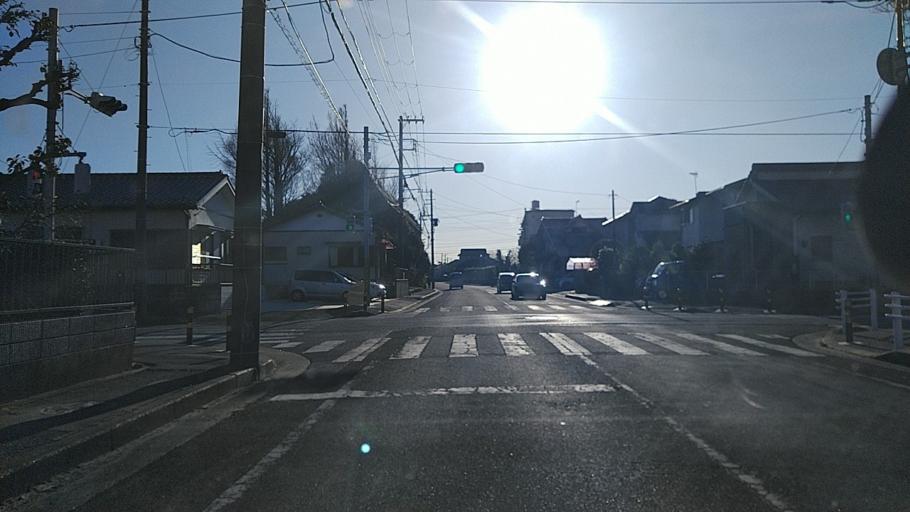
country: JP
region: Chiba
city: Kimitsu
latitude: 35.3299
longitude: 139.8898
